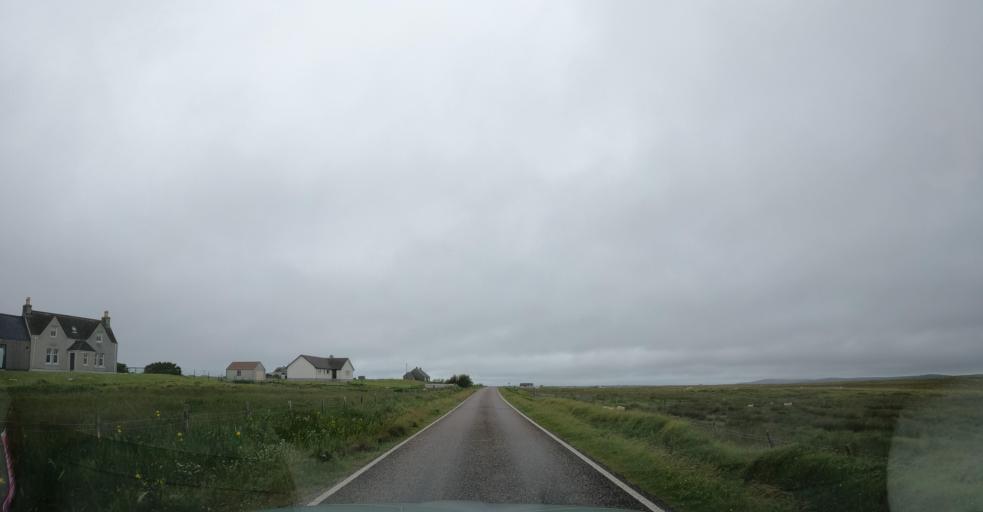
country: GB
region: Scotland
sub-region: Eilean Siar
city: Isle of North Uist
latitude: 57.5567
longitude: -7.3557
